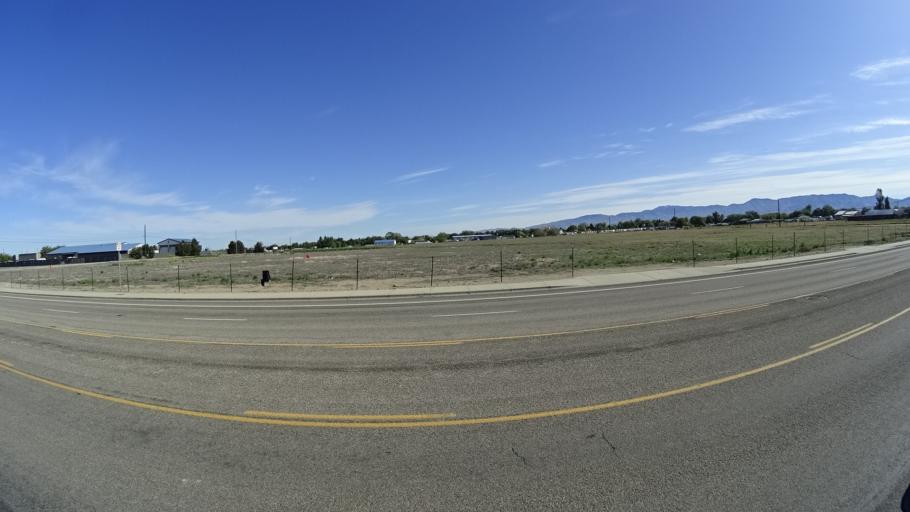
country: US
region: Idaho
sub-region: Ada County
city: Garden City
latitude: 43.5754
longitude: -116.2580
